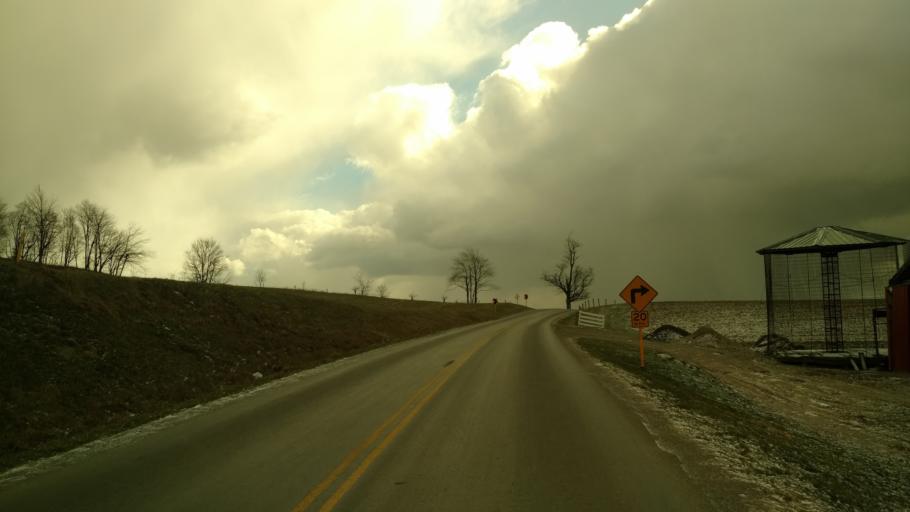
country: US
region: Ohio
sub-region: Tuscarawas County
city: Sugarcreek
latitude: 40.4855
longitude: -81.7866
